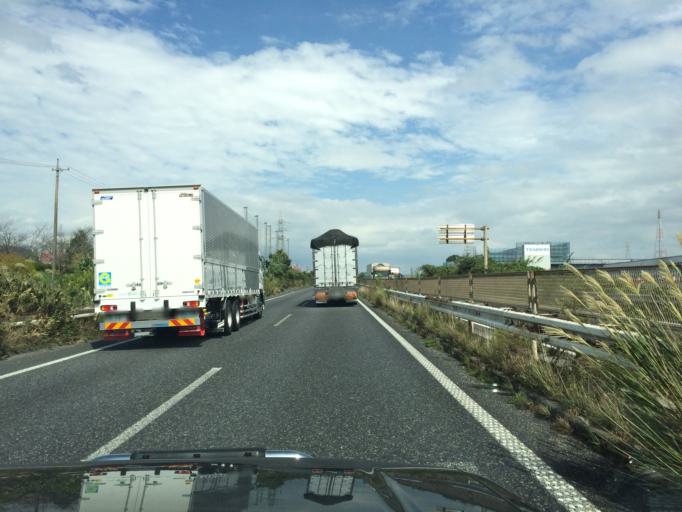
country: JP
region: Mie
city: Ueno-ebisumachi
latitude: 34.7173
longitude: 136.0811
